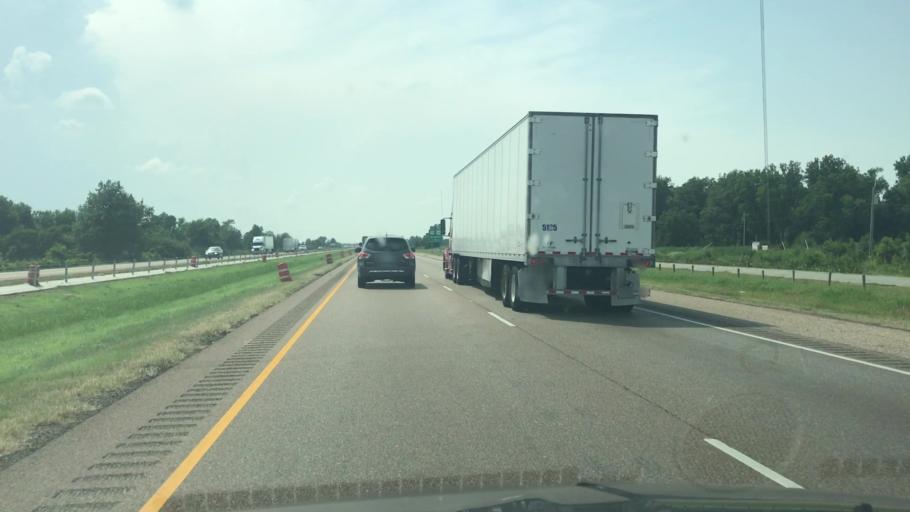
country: US
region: Arkansas
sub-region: Crittenden County
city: Earle
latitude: 35.1506
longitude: -90.3771
